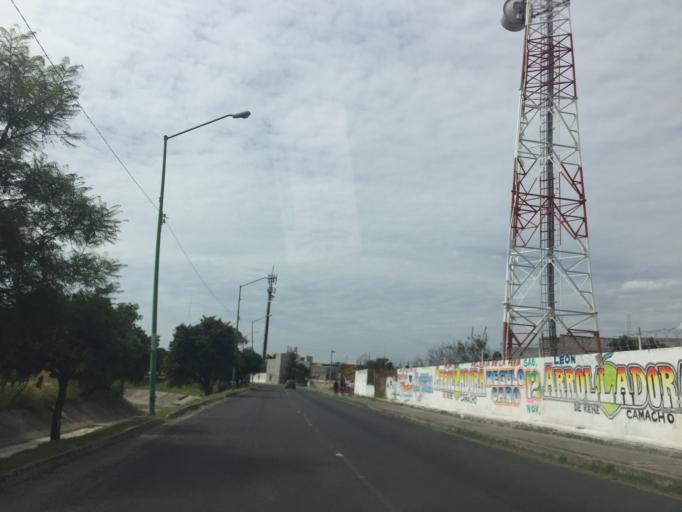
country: MX
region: Guanajuato
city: Leon
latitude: 21.0999
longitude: -101.6641
